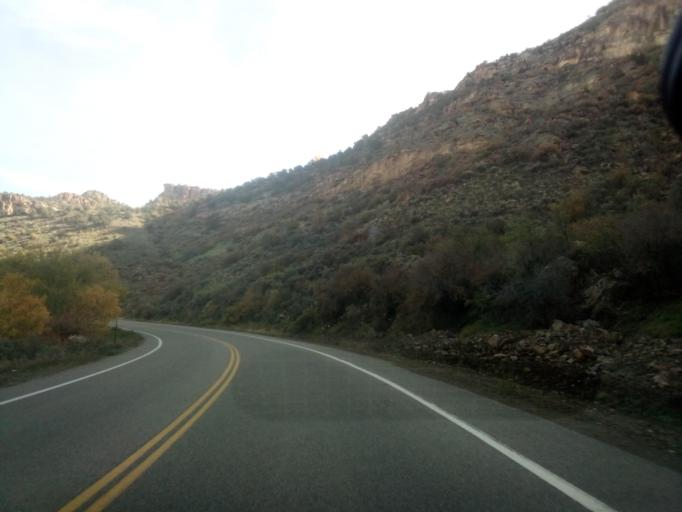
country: US
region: Colorado
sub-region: Mesa County
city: Palisade
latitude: 39.1774
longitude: -108.2771
